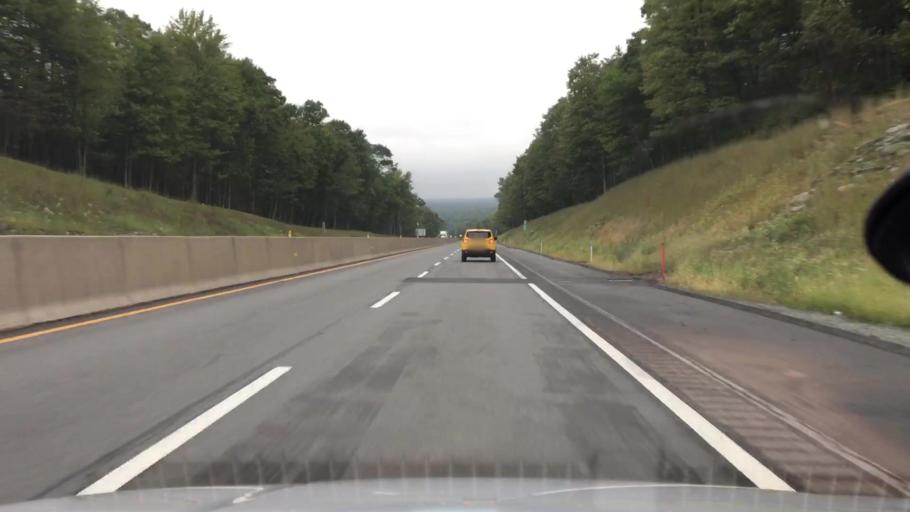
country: US
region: Pennsylvania
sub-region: Luzerne County
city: White Haven
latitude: 41.0887
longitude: -75.7389
